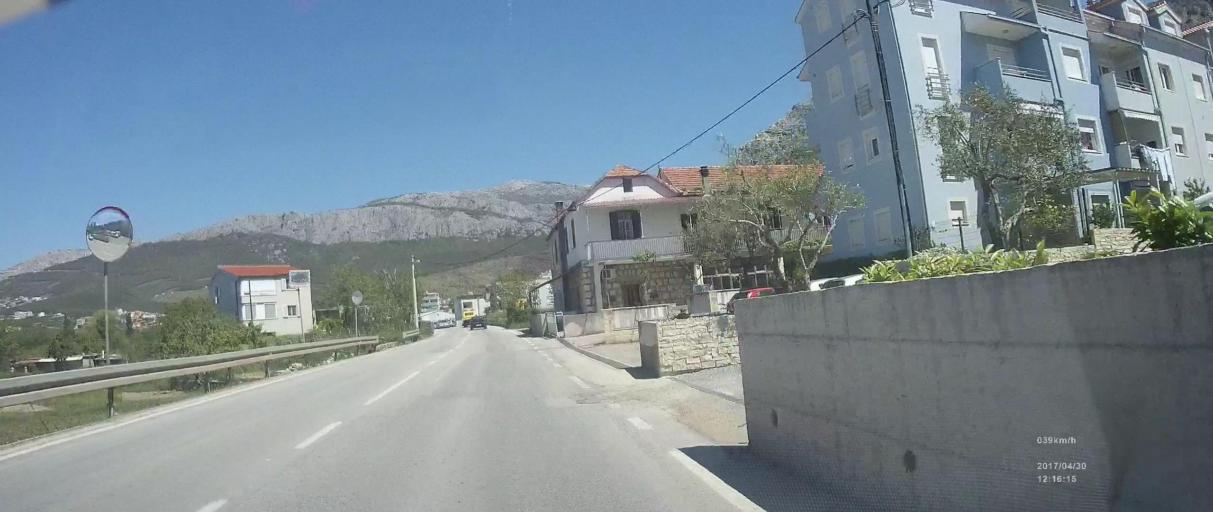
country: HR
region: Splitsko-Dalmatinska
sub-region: Grad Split
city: Stobrec
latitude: 43.5098
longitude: 16.5385
